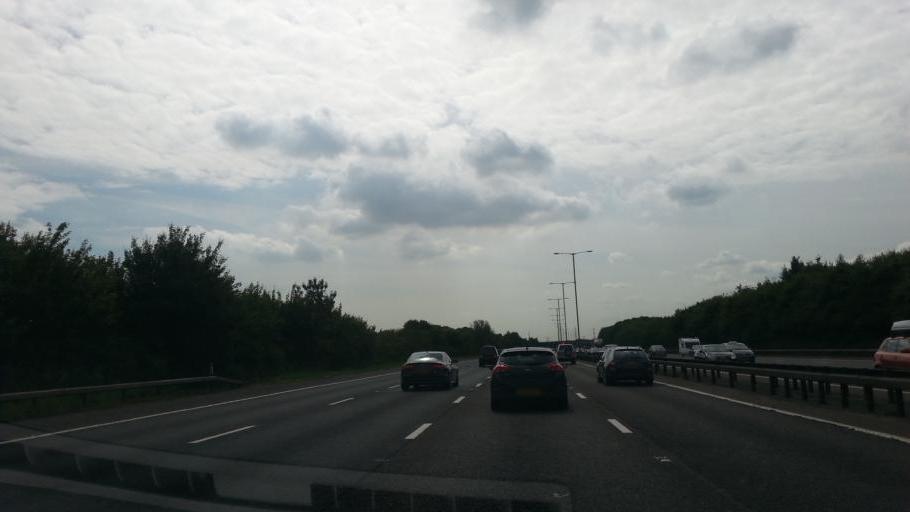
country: GB
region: England
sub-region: Greater London
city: Uxbridge
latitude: 51.5344
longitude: -0.4997
